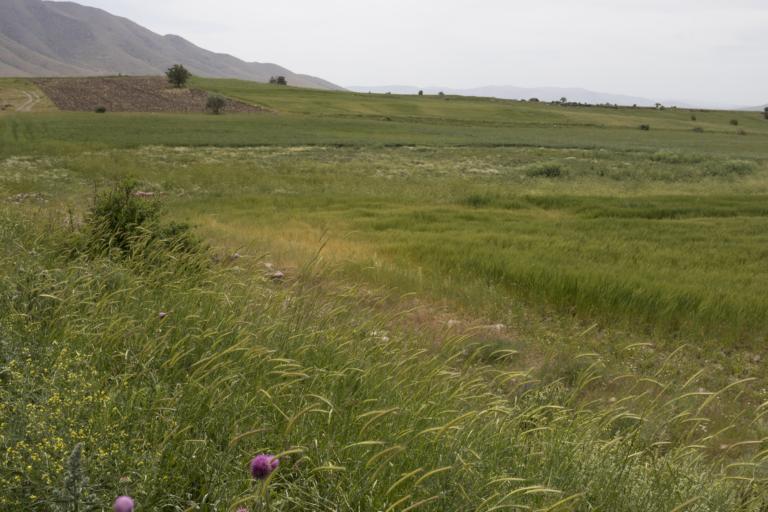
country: TR
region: Kayseri
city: Toklar
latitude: 38.4195
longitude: 36.0840
